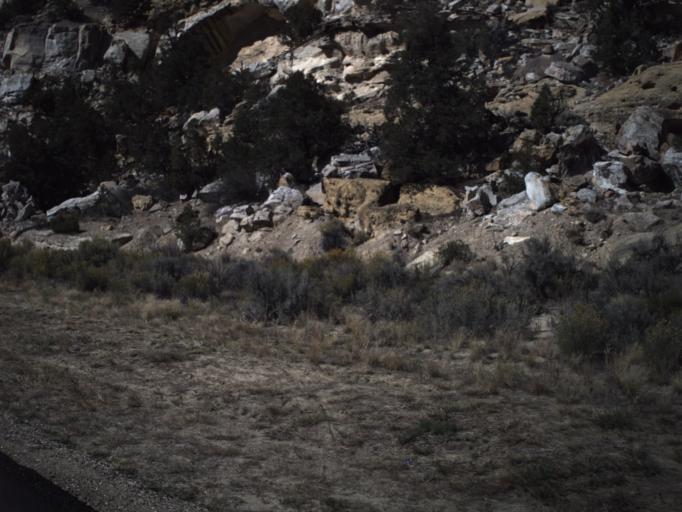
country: US
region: Utah
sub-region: Wayne County
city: Loa
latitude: 37.7382
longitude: -111.7383
